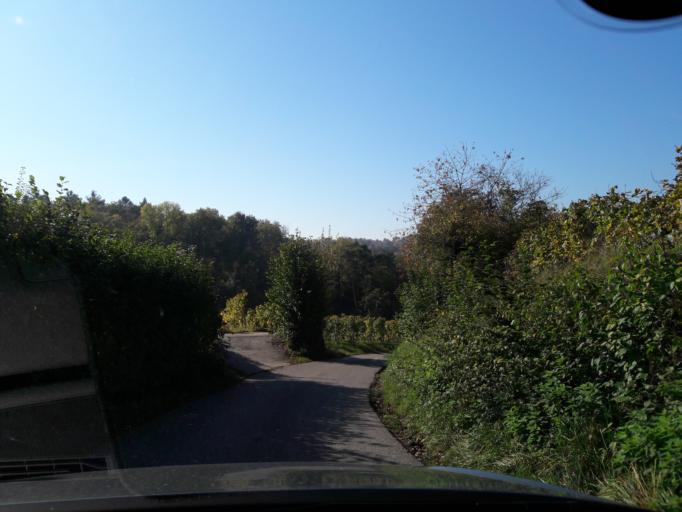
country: DE
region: Baden-Wuerttemberg
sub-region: Regierungsbezirk Stuttgart
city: Oedheim
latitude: 49.2093
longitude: 9.2694
